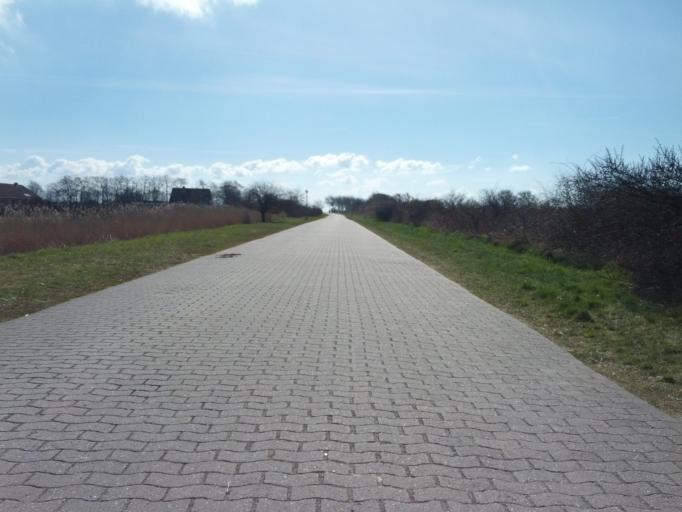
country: DE
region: Lower Saxony
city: Langeoog
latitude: 53.7324
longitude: 7.4948
